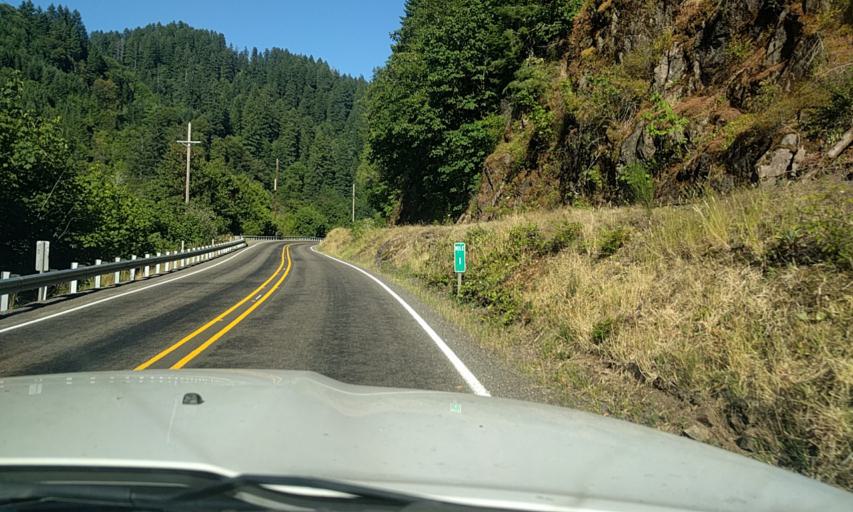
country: US
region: Oregon
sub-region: Lane County
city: Florence
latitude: 44.0407
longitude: -123.8723
